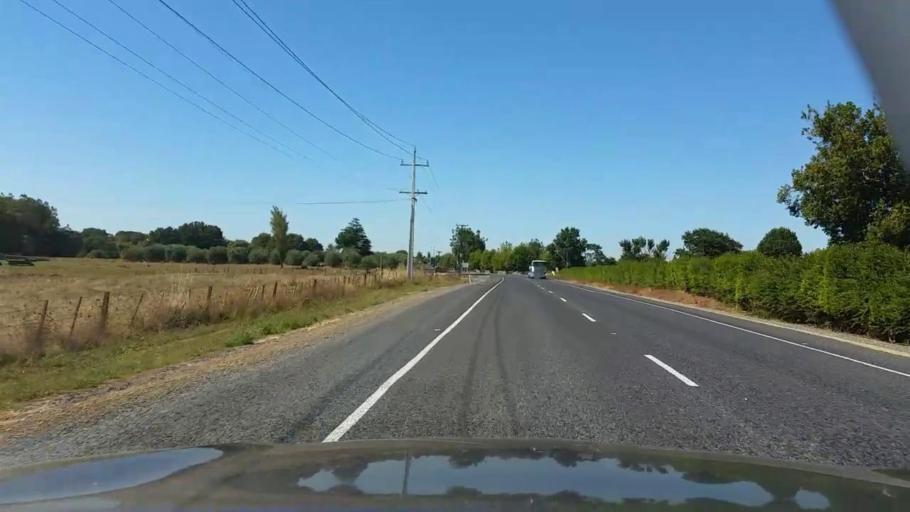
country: NZ
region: Waikato
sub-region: Hamilton City
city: Hamilton
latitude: -37.6664
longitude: 175.2999
